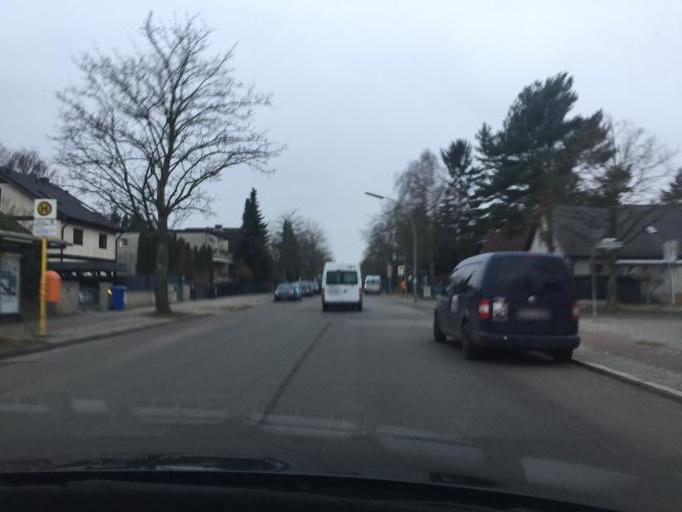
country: DE
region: Berlin
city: Lichtenrade
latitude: 52.4106
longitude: 13.4181
